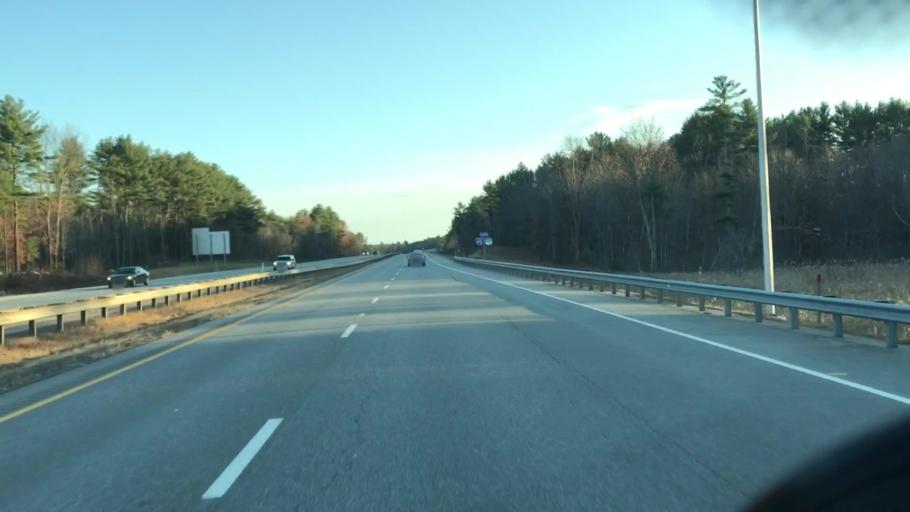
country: US
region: Maine
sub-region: Cumberland County
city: New Gloucester
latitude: 43.8777
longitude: -70.3328
